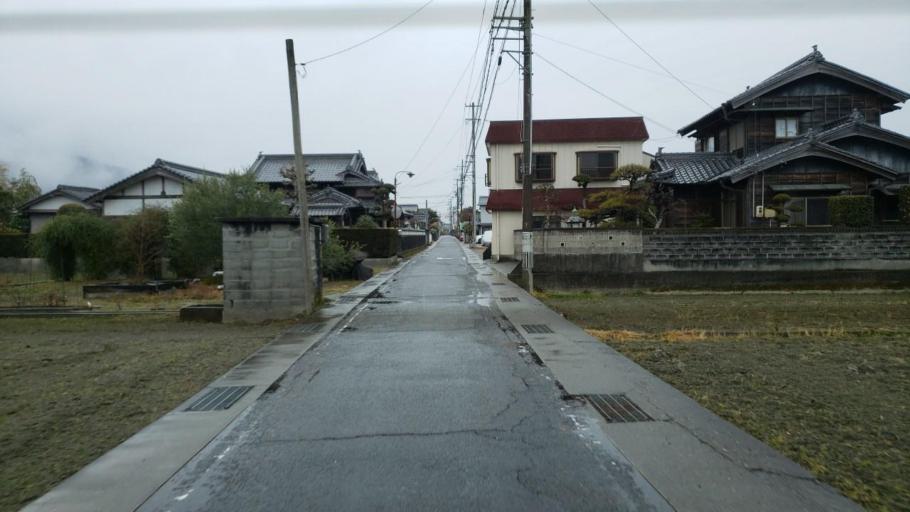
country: JP
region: Tokushima
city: Kamojimacho-jogejima
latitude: 34.0595
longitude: 134.2888
